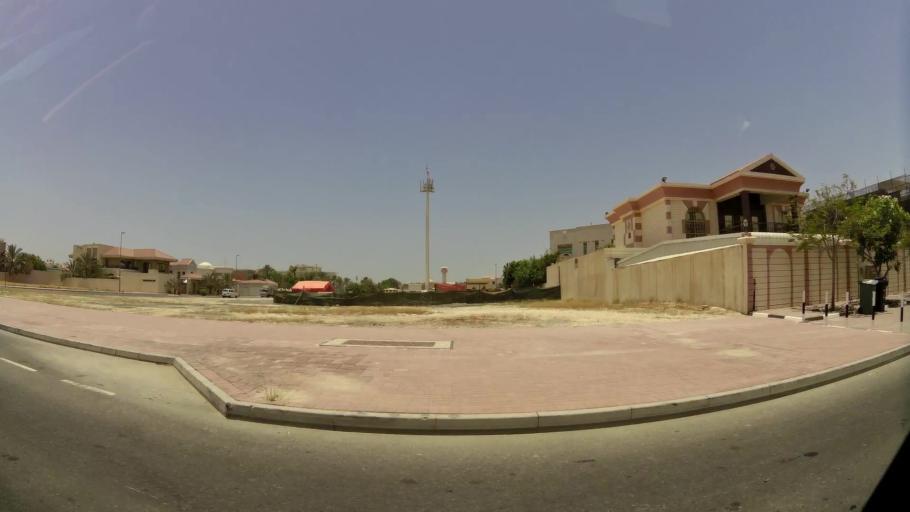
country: AE
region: Dubai
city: Dubai
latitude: 25.1801
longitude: 55.2310
